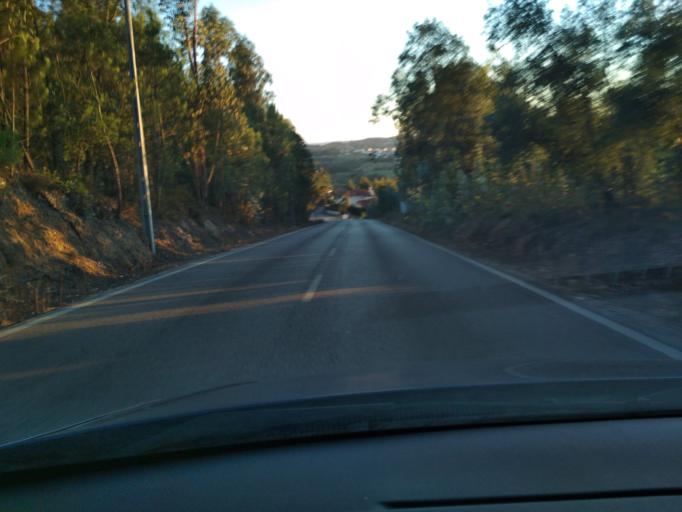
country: PT
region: Coimbra
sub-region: Coimbra
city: Coimbra
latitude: 40.1778
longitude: -8.4772
